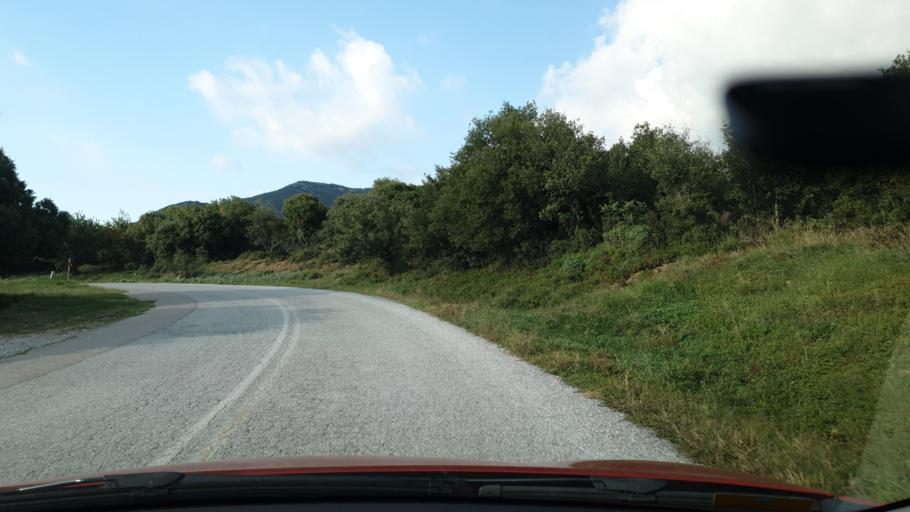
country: GR
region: Central Macedonia
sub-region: Nomos Thessalonikis
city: Peristera
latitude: 40.5244
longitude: 23.1876
